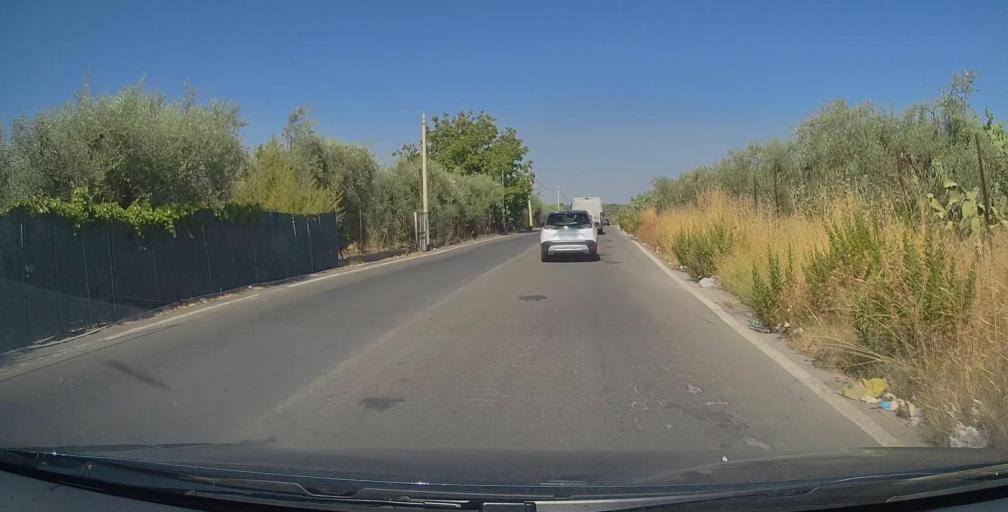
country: IT
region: Sicily
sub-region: Catania
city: Palazzolo
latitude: 37.5486
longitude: 14.9382
